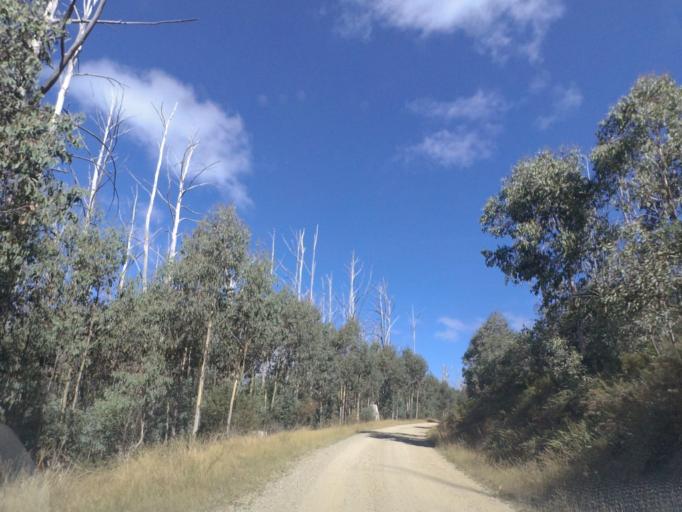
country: AU
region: Victoria
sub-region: Murrindindi
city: Alexandra
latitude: -37.4244
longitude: 145.8022
